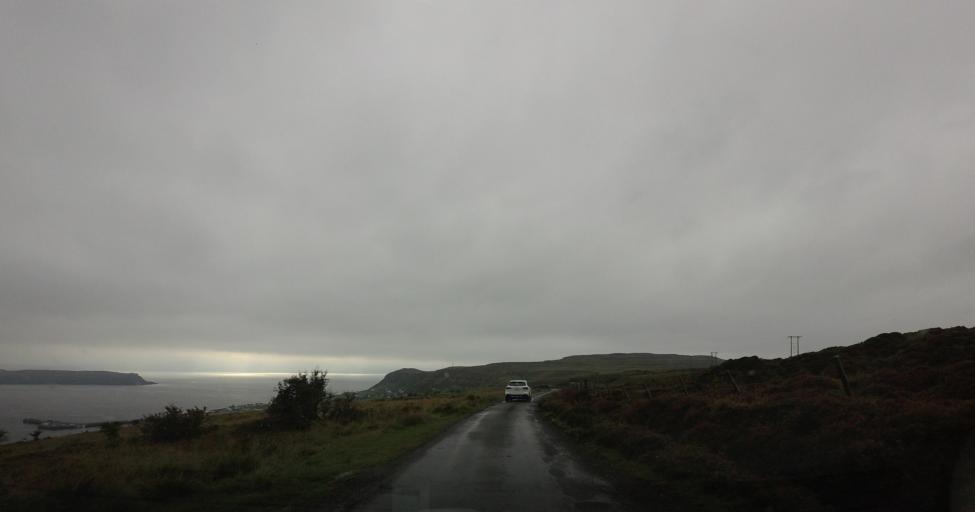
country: GB
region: Scotland
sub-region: Highland
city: Portree
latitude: 57.5942
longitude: -6.3640
